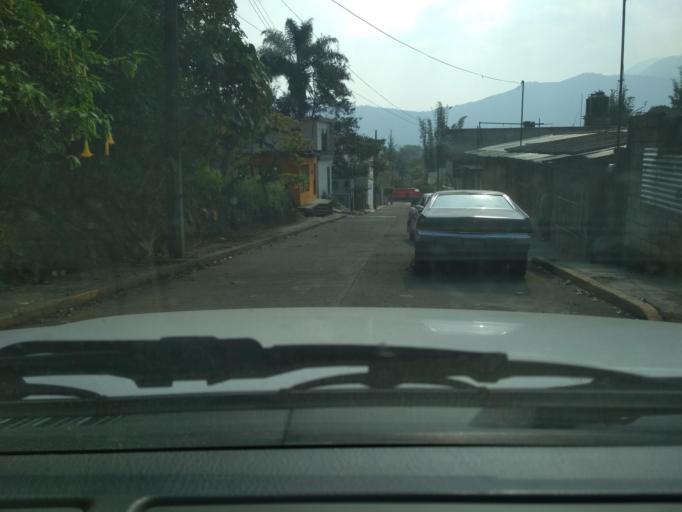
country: MX
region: Veracruz
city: Orizaba
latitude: 18.8706
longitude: -97.0921
